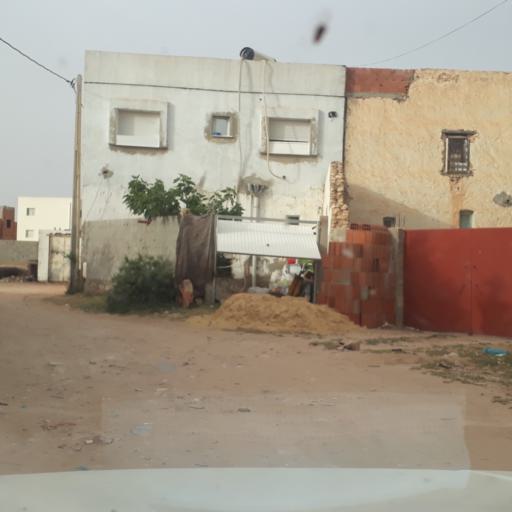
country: TN
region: Safaqis
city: Al Qarmadah
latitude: 34.8192
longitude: 10.7707
